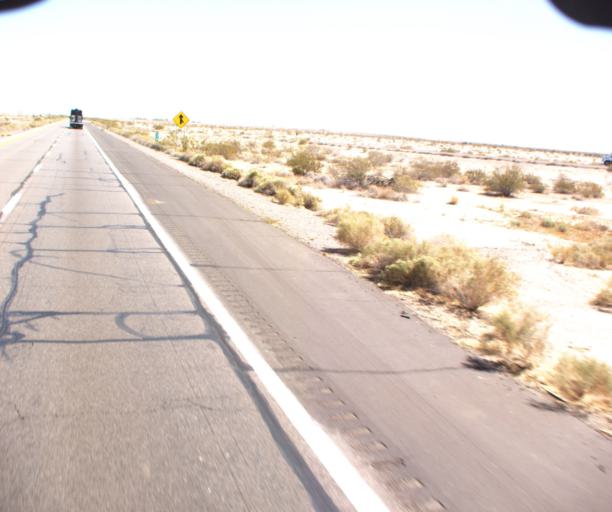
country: US
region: Arizona
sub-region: Yuma County
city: Wellton
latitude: 32.6814
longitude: -114.0220
